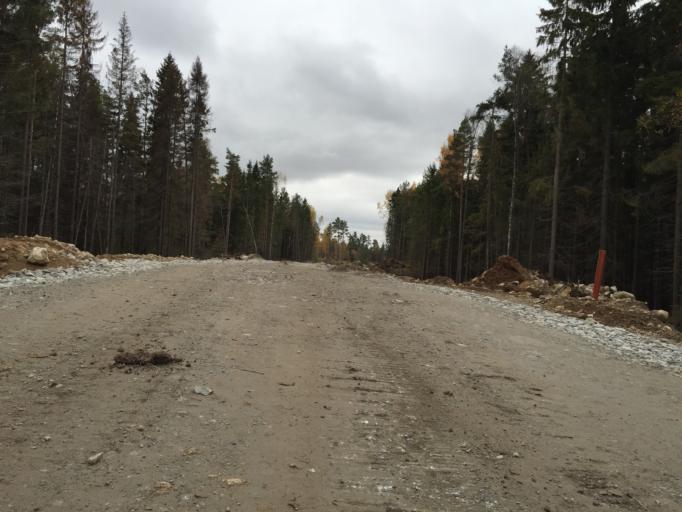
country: SE
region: Vaestmanland
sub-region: Hallstahammars Kommun
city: Hallstahammar
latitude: 59.6286
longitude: 16.2115
